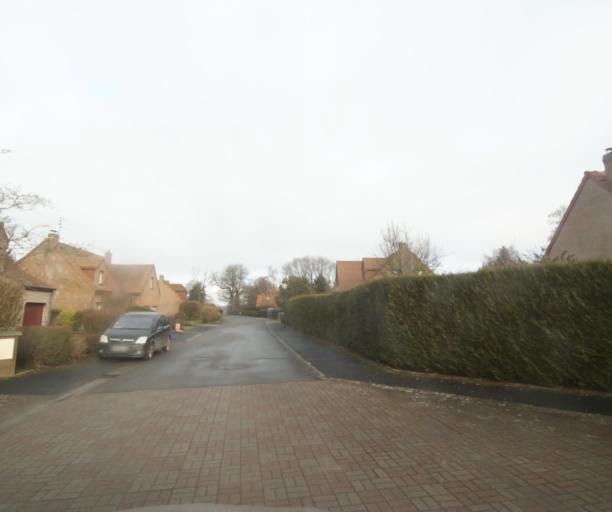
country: FR
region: Nord-Pas-de-Calais
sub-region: Departement du Nord
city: Famars
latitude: 50.2928
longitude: 3.5122
